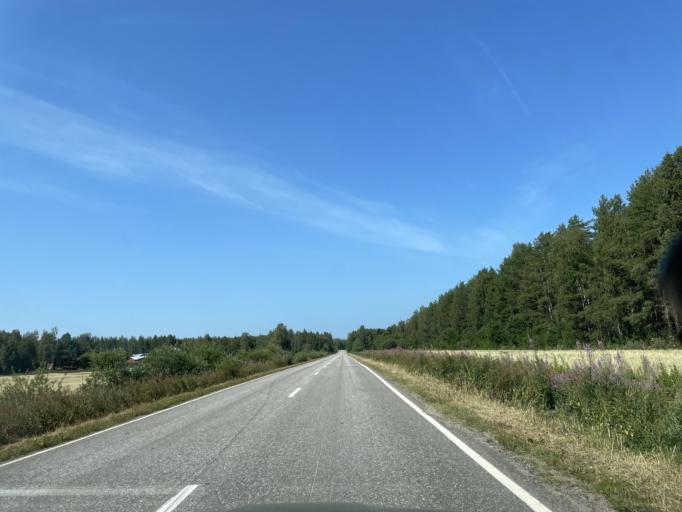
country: FI
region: Central Finland
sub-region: Saarijaervi-Viitasaari
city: Pihtipudas
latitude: 63.3646
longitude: 25.6460
